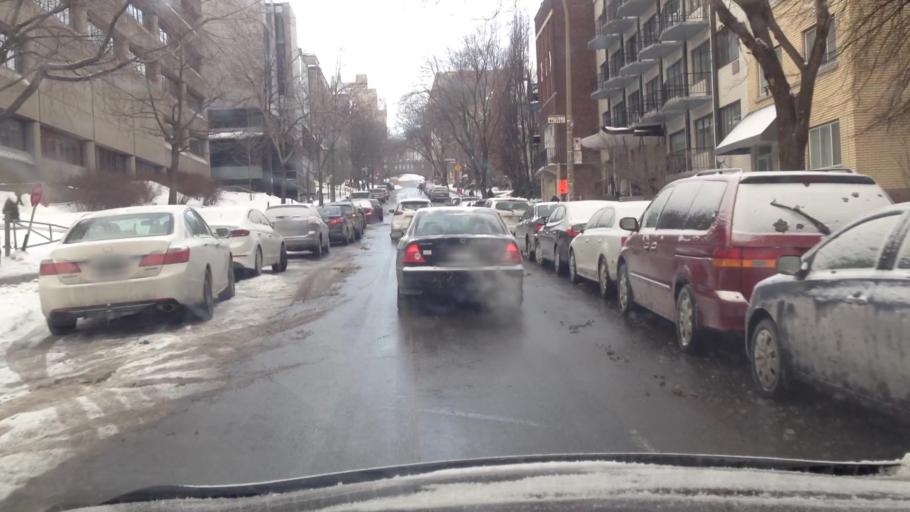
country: CA
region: Quebec
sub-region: Montreal
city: Montreal
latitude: 45.5070
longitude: -73.5775
